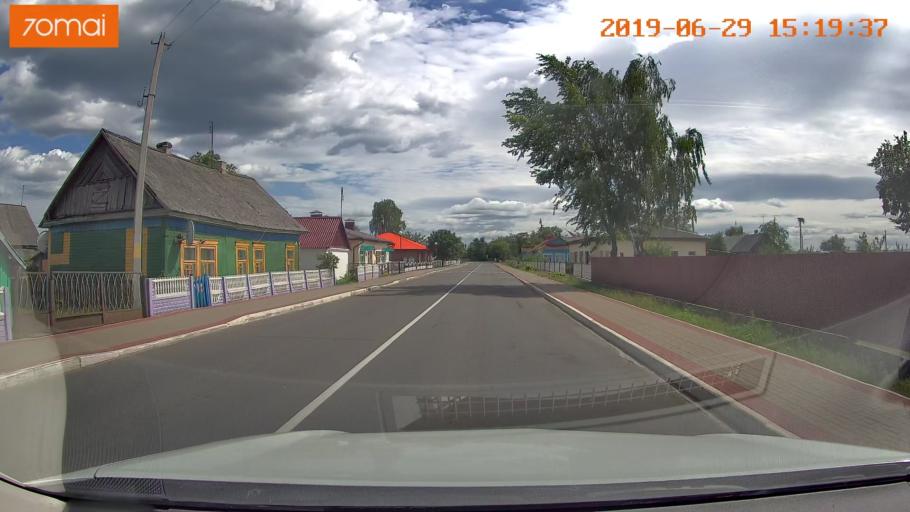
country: BY
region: Brest
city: Mikashevichy
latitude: 52.2189
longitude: 27.4697
